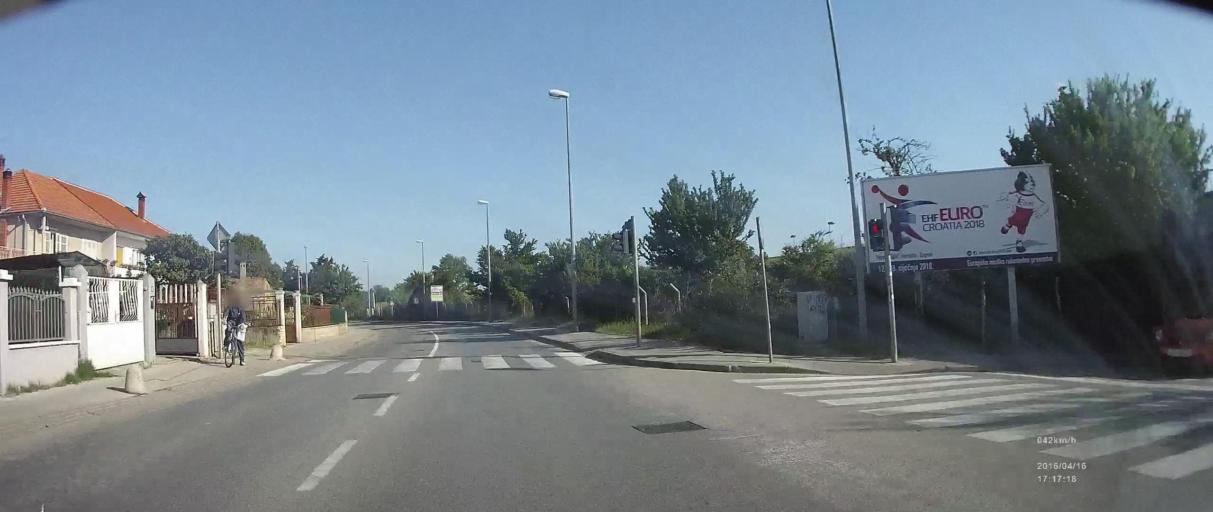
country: HR
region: Zadarska
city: Zadar
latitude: 44.1036
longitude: 15.2460
